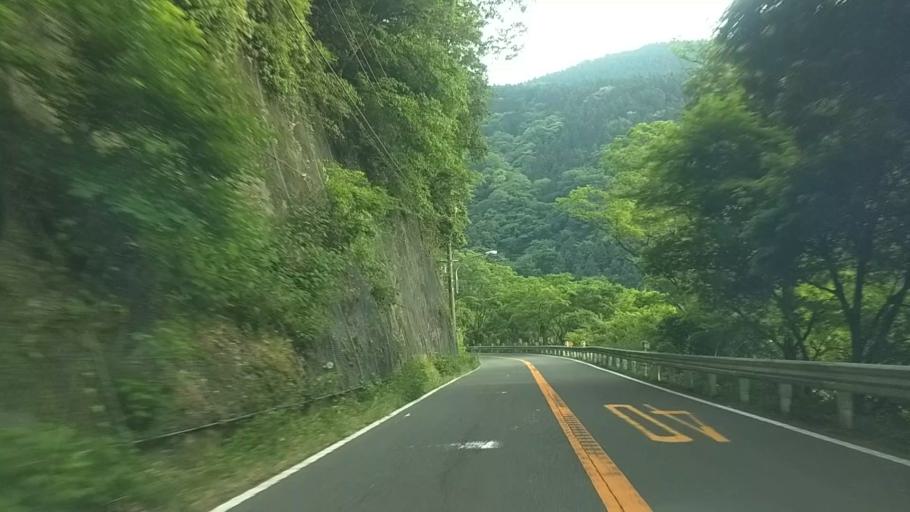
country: JP
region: Shizuoka
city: Gotemba
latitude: 35.3626
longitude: 139.0559
